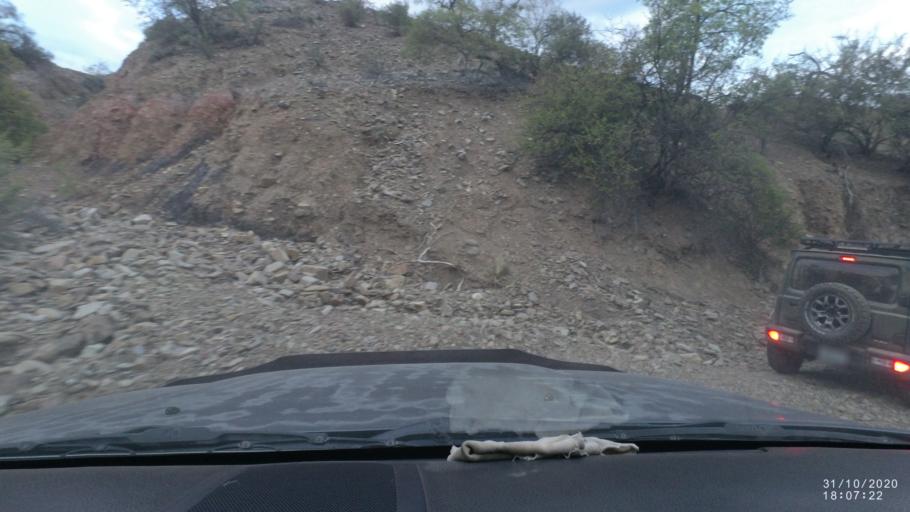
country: BO
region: Chuquisaca
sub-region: Provincia Zudanez
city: Mojocoya
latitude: -18.6652
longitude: -64.5282
